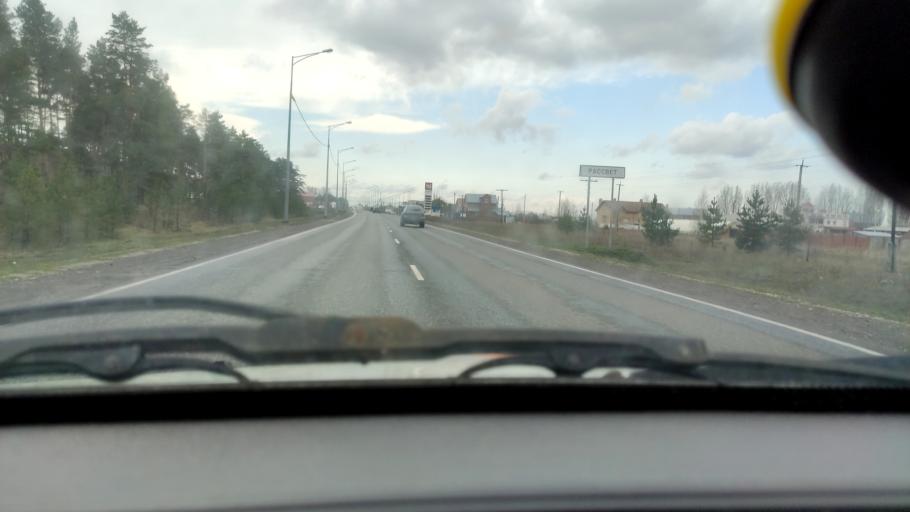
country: RU
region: Samara
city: Povolzhskiy
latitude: 53.5935
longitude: 49.5834
